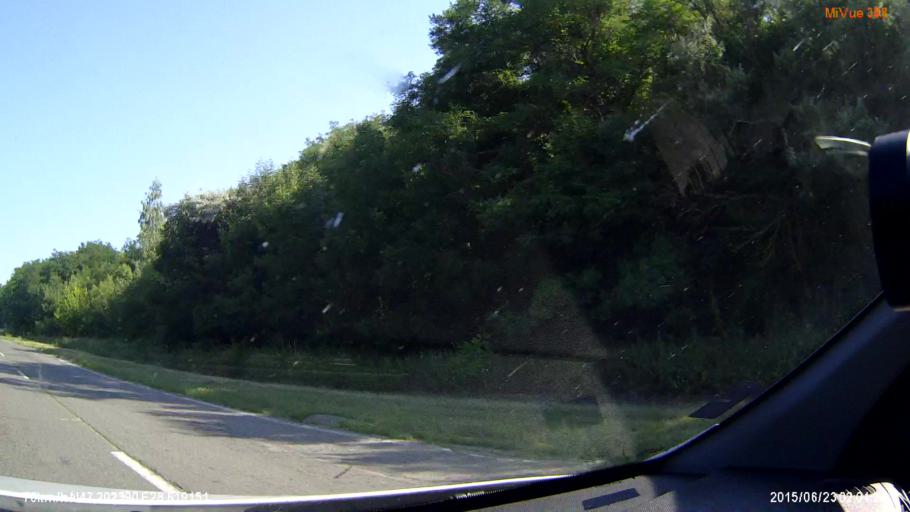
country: MD
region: Straseni
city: Straseni
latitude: 47.2027
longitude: 28.6188
